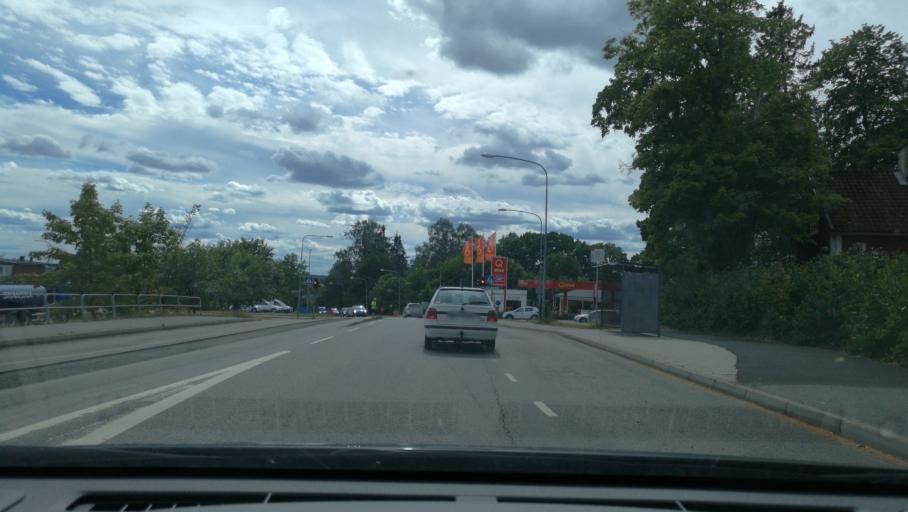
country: SE
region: OEstergoetland
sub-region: Norrkopings Kommun
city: Jursla
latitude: 58.6611
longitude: 16.1761
